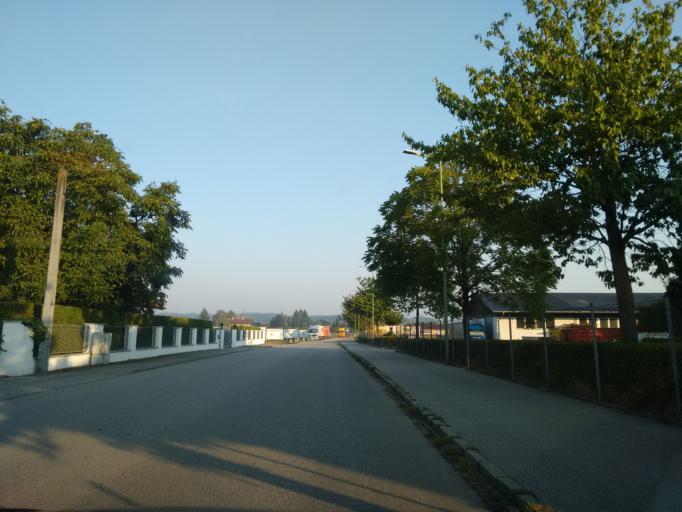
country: AT
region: Upper Austria
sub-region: Wels Stadt
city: Wels
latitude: 48.1773
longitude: 14.0128
